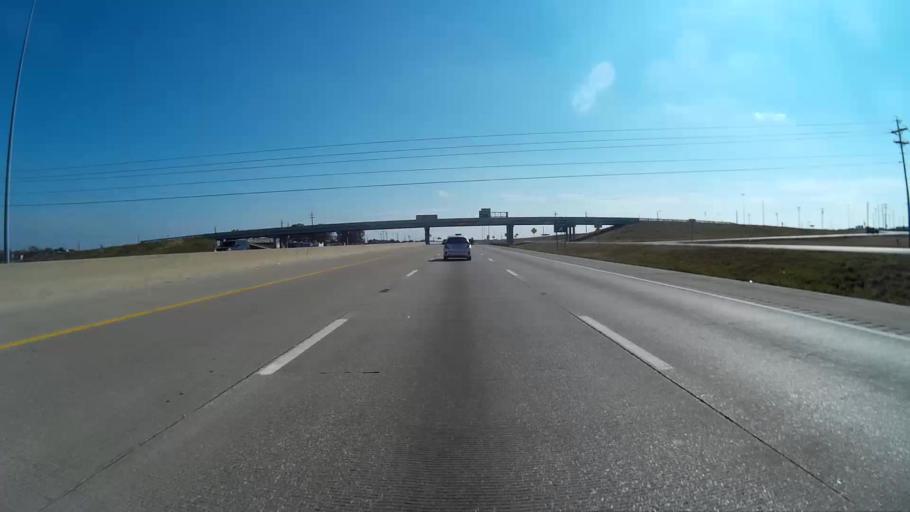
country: US
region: Texas
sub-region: Dallas County
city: Hutchins
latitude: 32.6338
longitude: -96.7001
